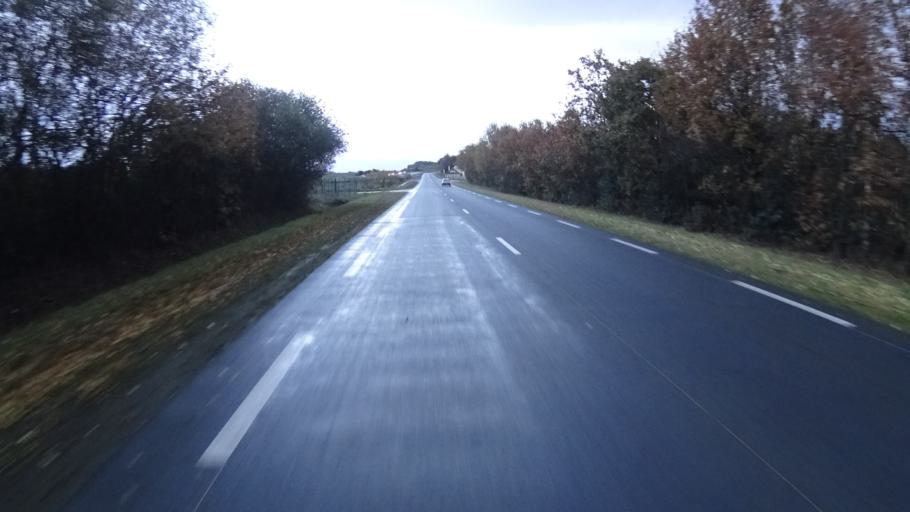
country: FR
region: Brittany
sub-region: Departement d'Ille-et-Vilaine
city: Bains-sur-Oust
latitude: 47.6930
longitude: -2.0448
